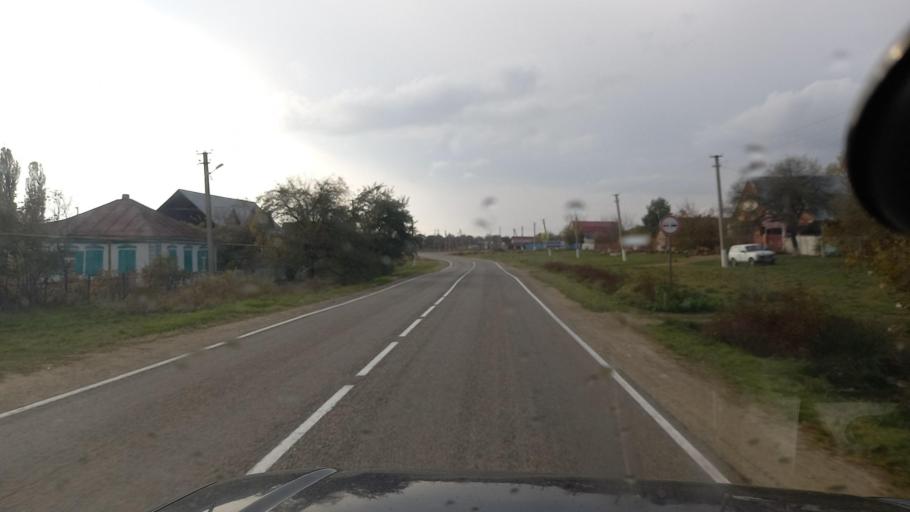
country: RU
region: Krasnodarskiy
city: Gubskaya
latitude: 44.3193
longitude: 40.6099
